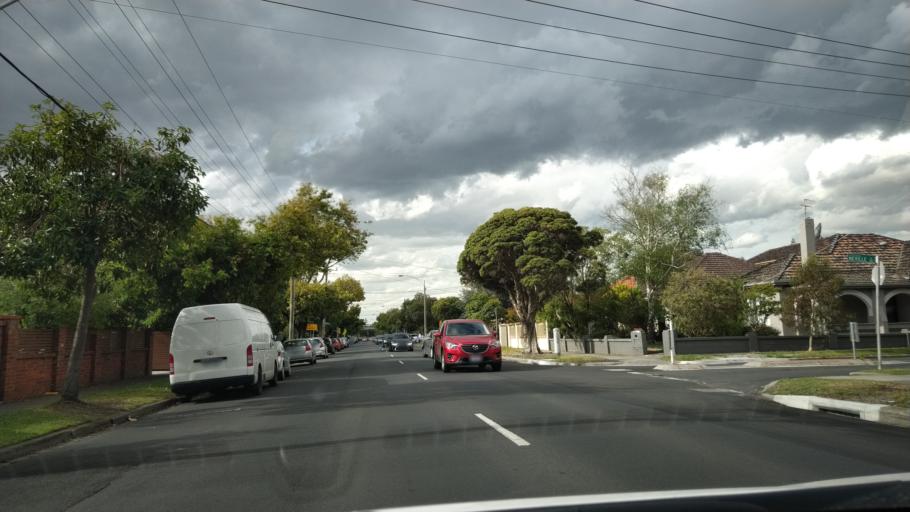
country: AU
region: Victoria
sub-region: Glen Eira
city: Glen Huntly
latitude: -37.8973
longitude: 145.0453
